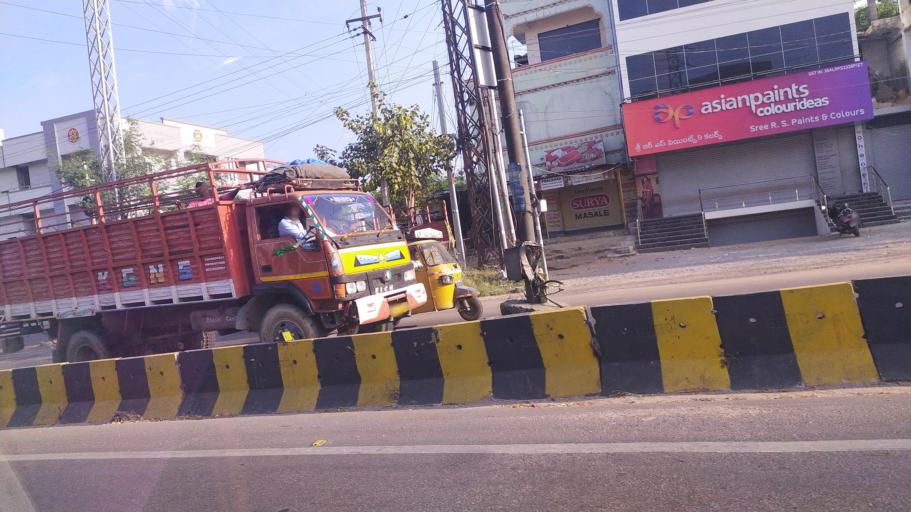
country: IN
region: Telangana
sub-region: Rangareddi
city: Balapur
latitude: 17.3199
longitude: 78.4344
